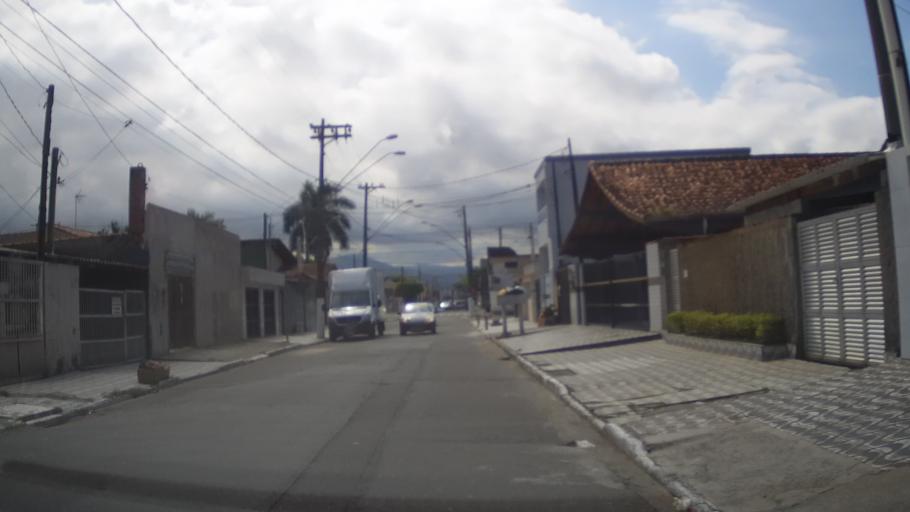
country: BR
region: Sao Paulo
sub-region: Praia Grande
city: Praia Grande
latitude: -24.0167
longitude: -46.4516
